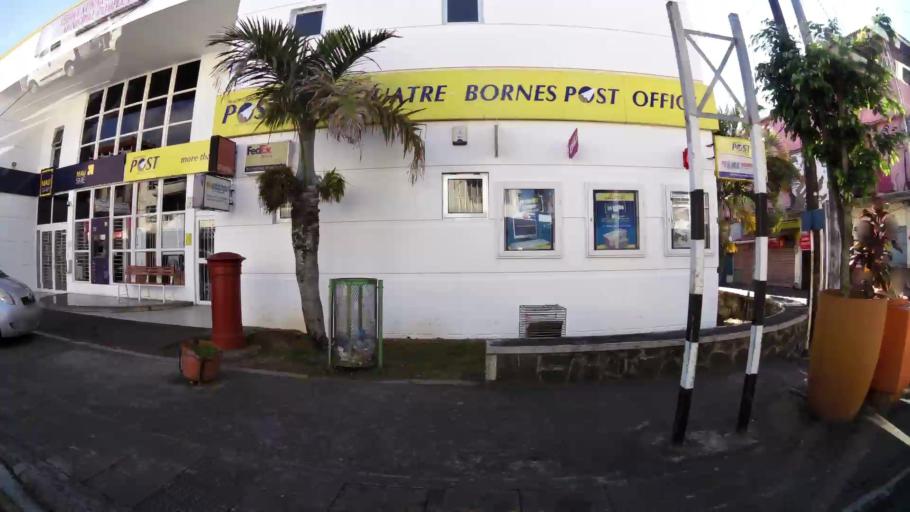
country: MU
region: Plaines Wilhems
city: Quatre Bornes
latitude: -20.2649
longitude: 57.4798
